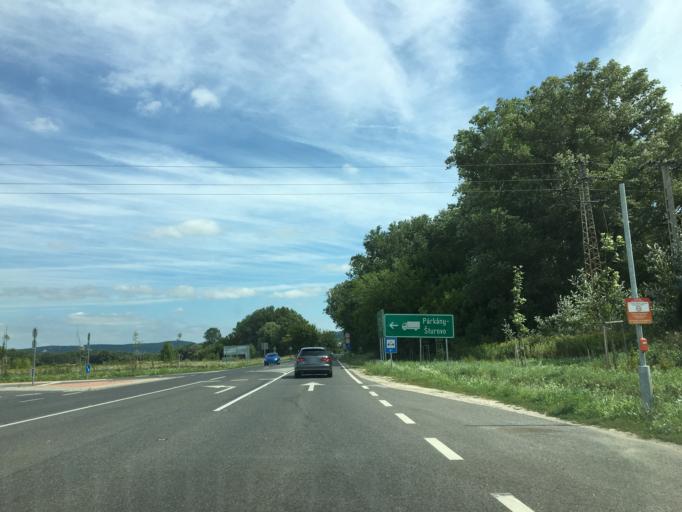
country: SK
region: Nitriansky
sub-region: Okres Nove Zamky
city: Sturovo
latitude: 47.7702
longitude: 18.7132
